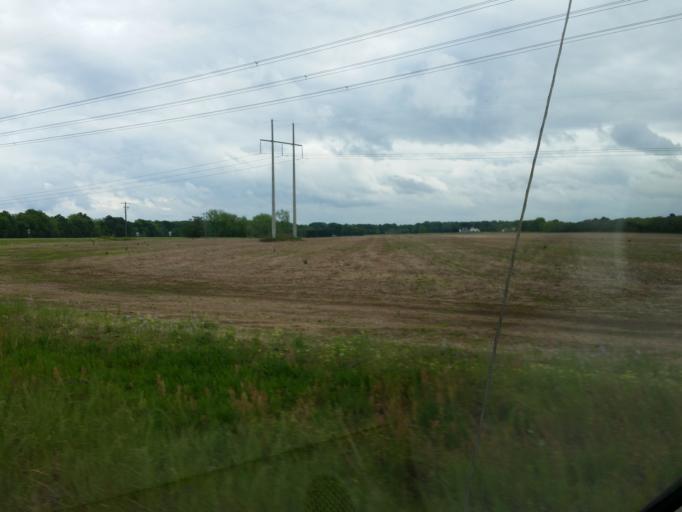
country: US
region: Georgia
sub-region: Peach County
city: Byron
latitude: 32.6642
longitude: -83.8073
